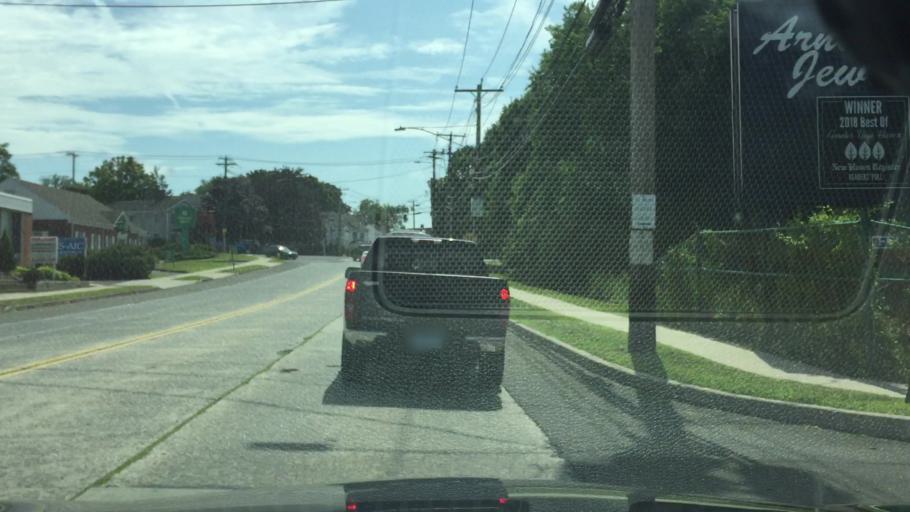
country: US
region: Connecticut
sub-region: New Haven County
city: Milford
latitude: 41.2282
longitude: -73.0506
